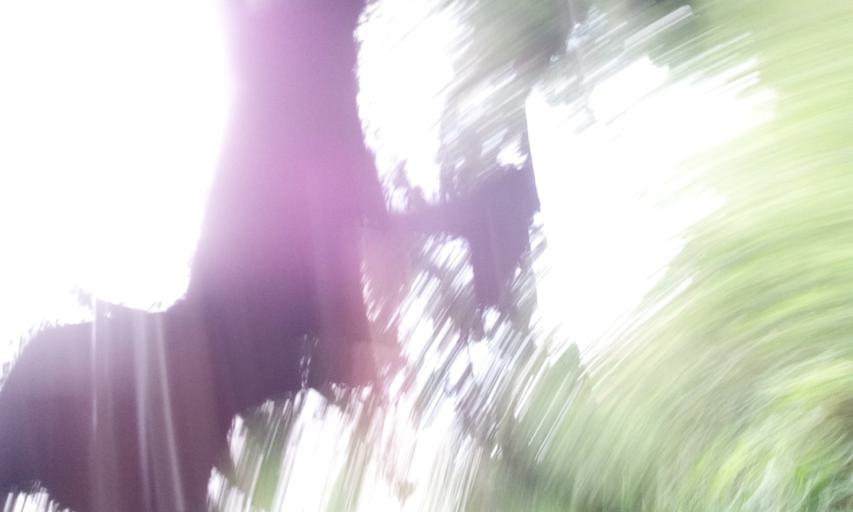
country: FR
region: Lower Normandy
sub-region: Departement du Calvados
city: Creully
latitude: 49.2885
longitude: -0.5102
